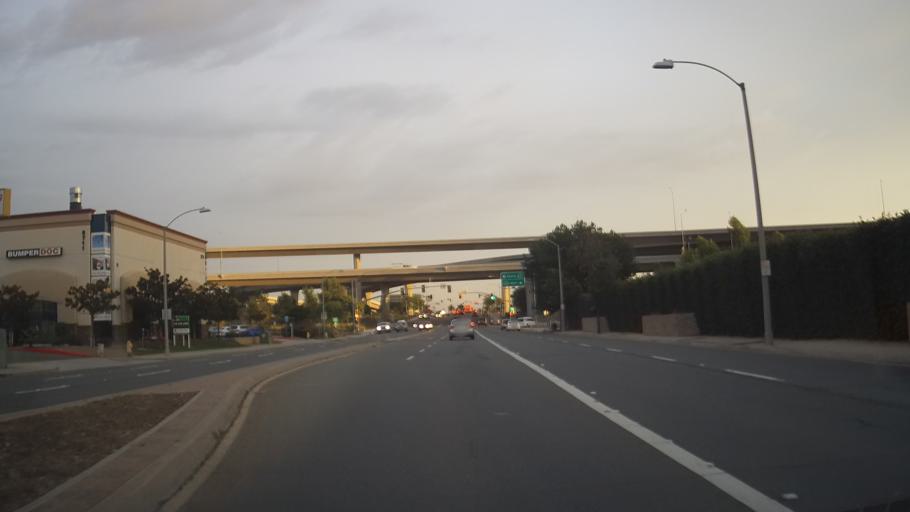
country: US
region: California
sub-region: San Diego County
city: Santee
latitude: 32.8343
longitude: -116.9650
